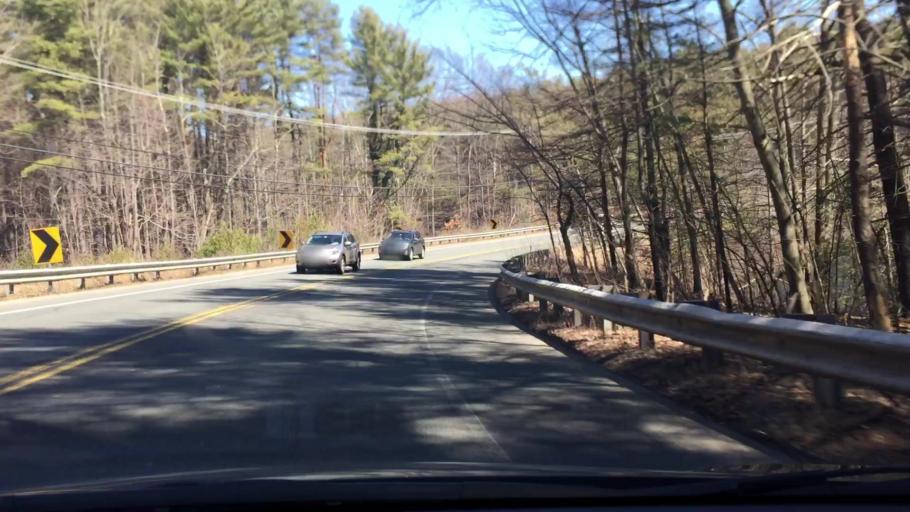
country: US
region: Massachusetts
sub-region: Hampden County
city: Holyoke
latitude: 42.1861
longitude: -72.6600
